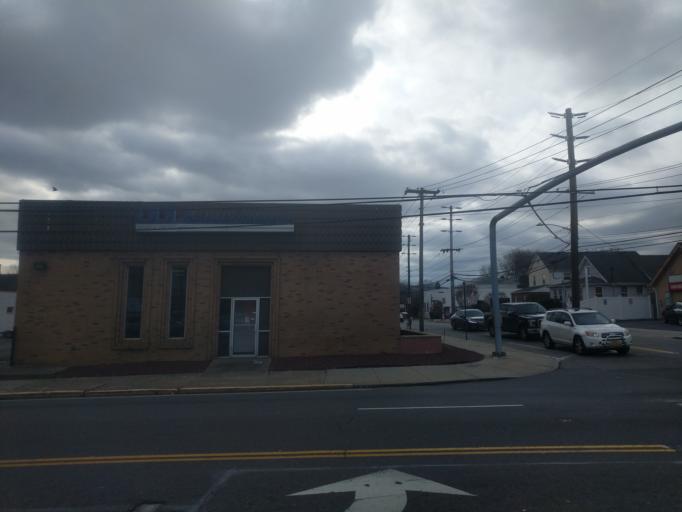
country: US
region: New York
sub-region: Nassau County
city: Lynbrook
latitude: 40.6619
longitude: -73.6878
